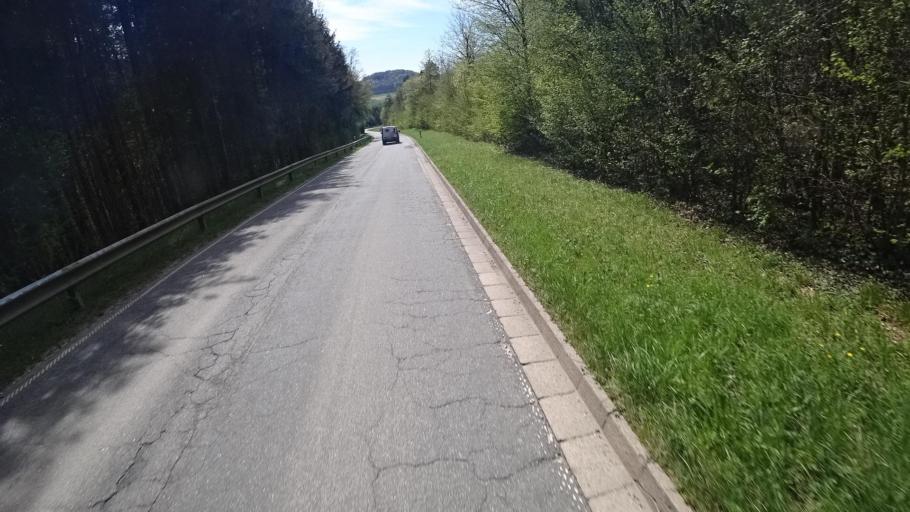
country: DE
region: Rheinland-Pfalz
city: Ralingen
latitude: 49.8188
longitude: 6.5260
